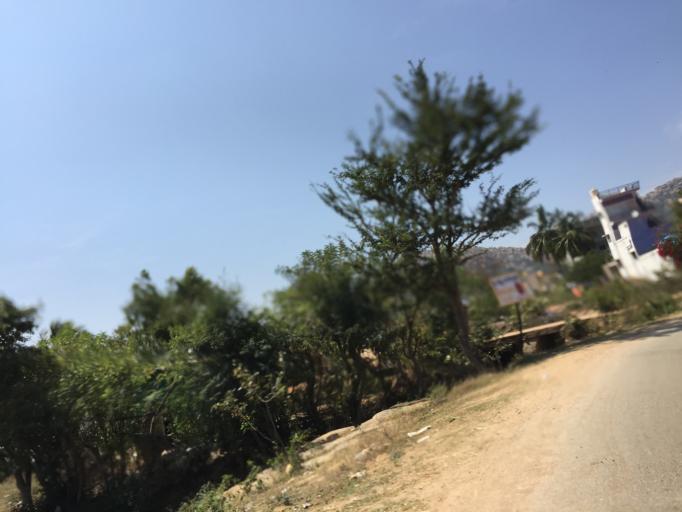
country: IN
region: Karnataka
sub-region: Kolar
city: Kolar
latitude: 13.1372
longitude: 78.1135
